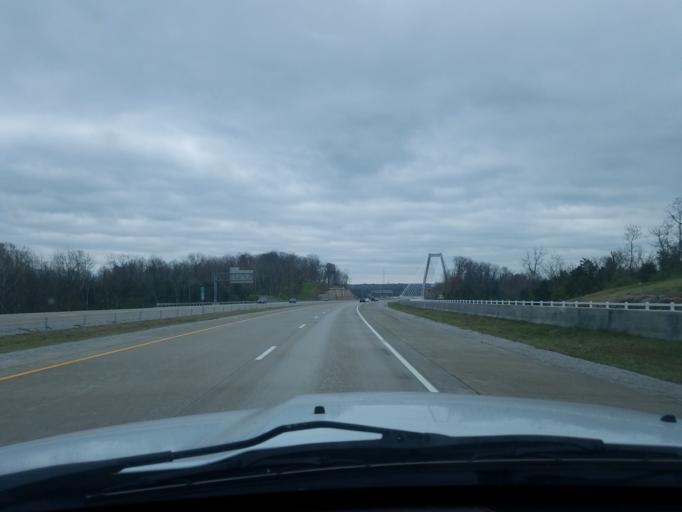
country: US
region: Kentucky
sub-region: Jefferson County
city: Prospect
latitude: 38.3481
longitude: -85.6515
